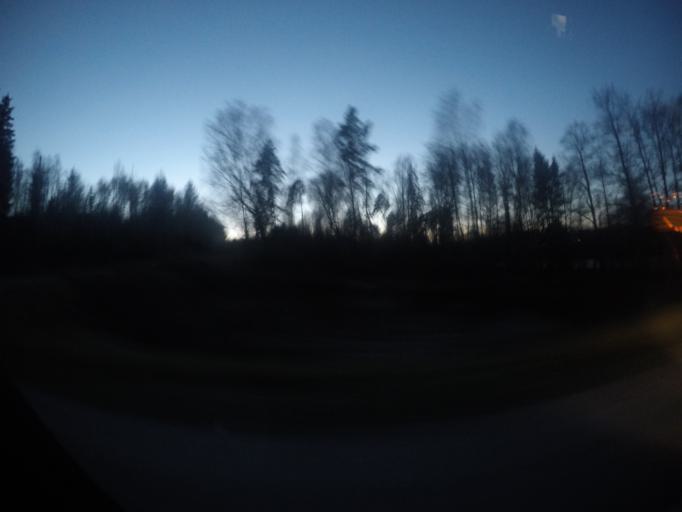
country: SE
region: Vaestmanland
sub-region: Arboga Kommun
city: Arboga
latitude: 59.4070
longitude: 15.7355
